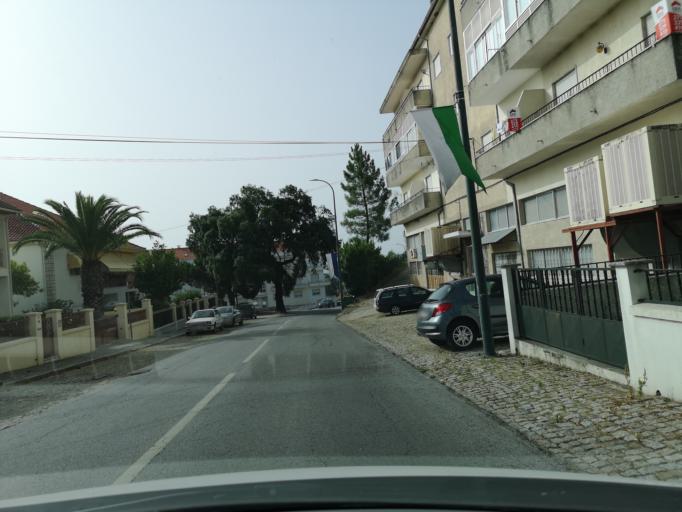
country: PT
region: Castelo Branco
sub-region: Belmonte
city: Belmonte
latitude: 40.3536
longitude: -7.3526
